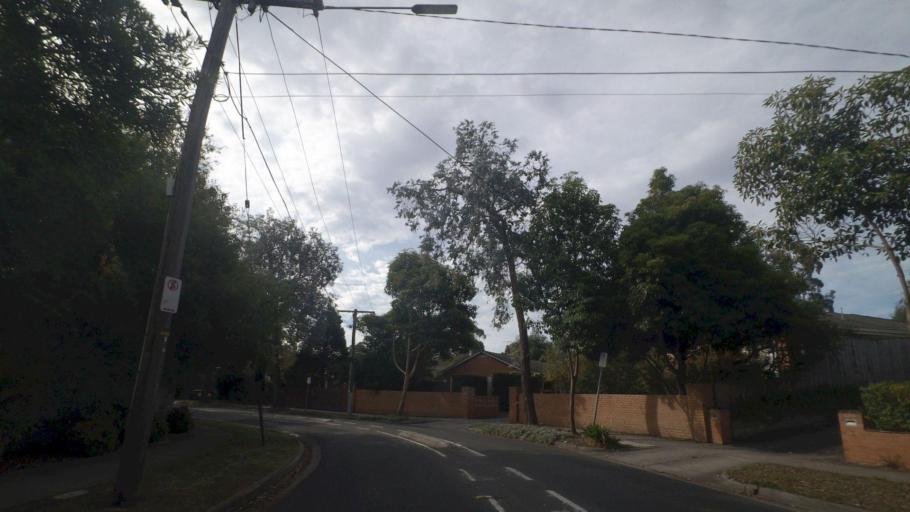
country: AU
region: Victoria
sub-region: Whitehorse
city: Blackburn
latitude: -37.8220
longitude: 145.1421
